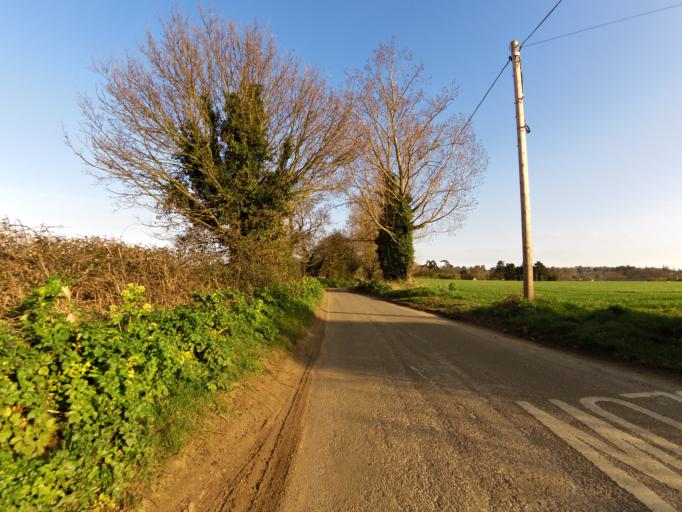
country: GB
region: England
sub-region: Suffolk
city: Kesgrave
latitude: 52.0881
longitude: 1.2495
